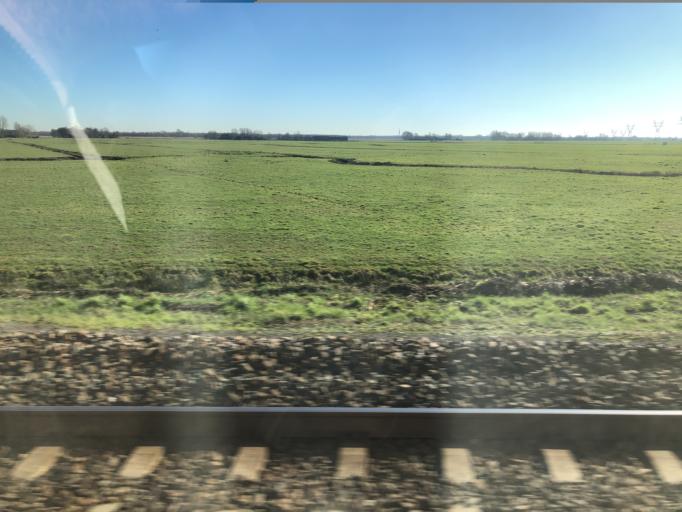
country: NL
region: North Holland
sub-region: Gemeente Weesp
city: Weesp
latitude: 52.3134
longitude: 5.0808
